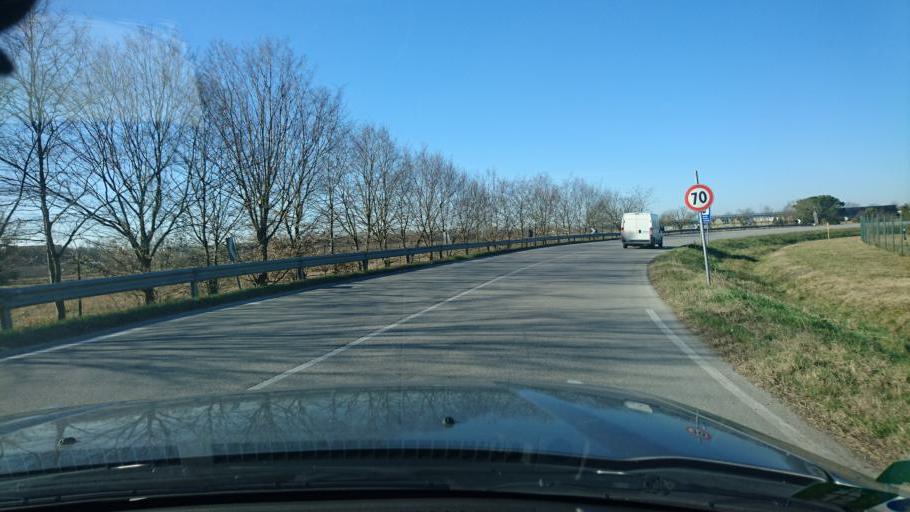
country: IT
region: Veneto
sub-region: Provincia di Rovigo
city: Porto Tolle
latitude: 44.9431
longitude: 12.3235
